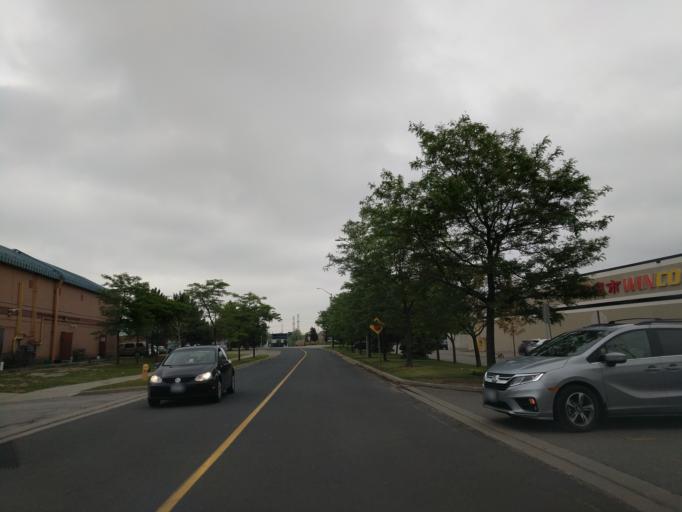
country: CA
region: Ontario
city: Markham
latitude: 43.8487
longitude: -79.3508
